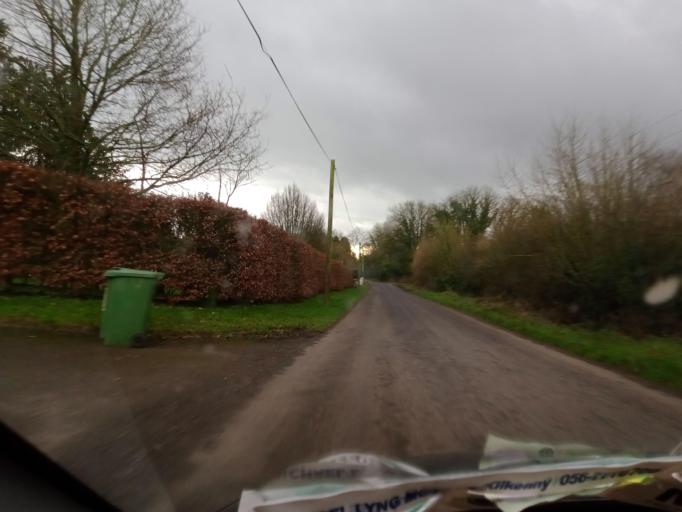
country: IE
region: Munster
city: Fethard
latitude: 52.5486
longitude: -7.7620
